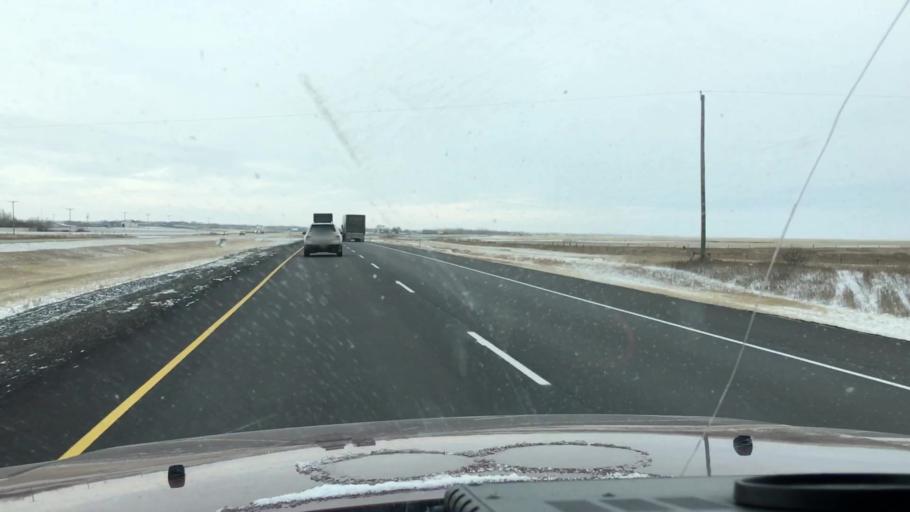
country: CA
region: Saskatchewan
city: Saskatoon
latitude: 51.7848
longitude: -106.4798
